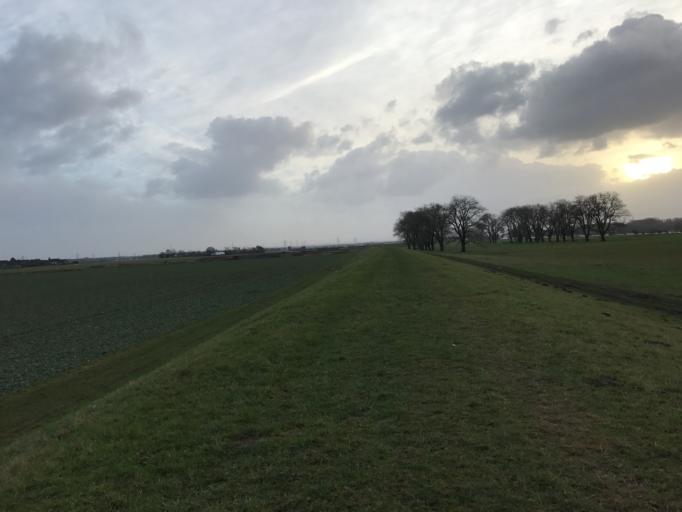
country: DE
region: North Rhine-Westphalia
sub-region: Regierungsbezirk Dusseldorf
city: Krefeld
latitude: 51.3499
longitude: 6.6729
